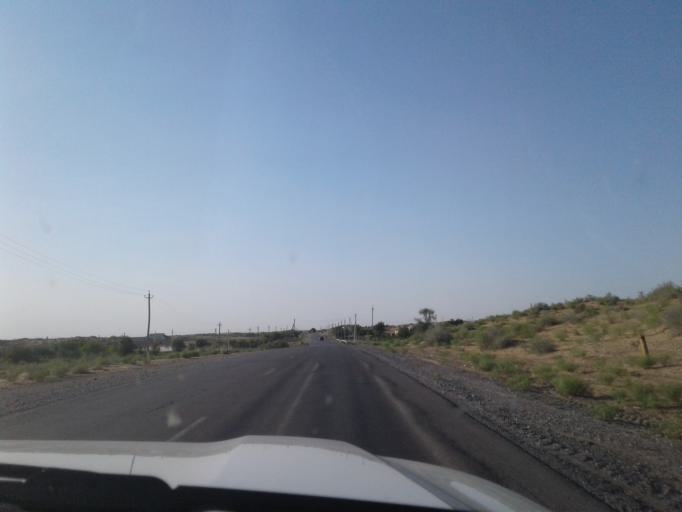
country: TM
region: Mary
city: Yoloeten
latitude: 37.2319
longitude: 62.3729
